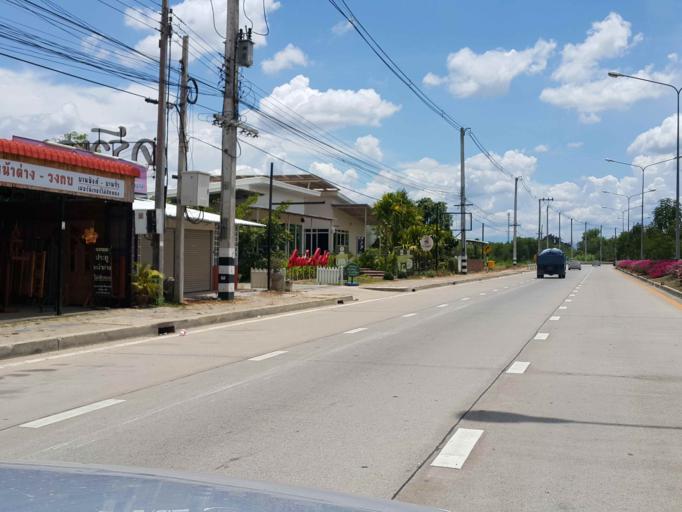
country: TH
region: Chiang Mai
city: Saraphi
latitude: 18.7425
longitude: 99.0037
